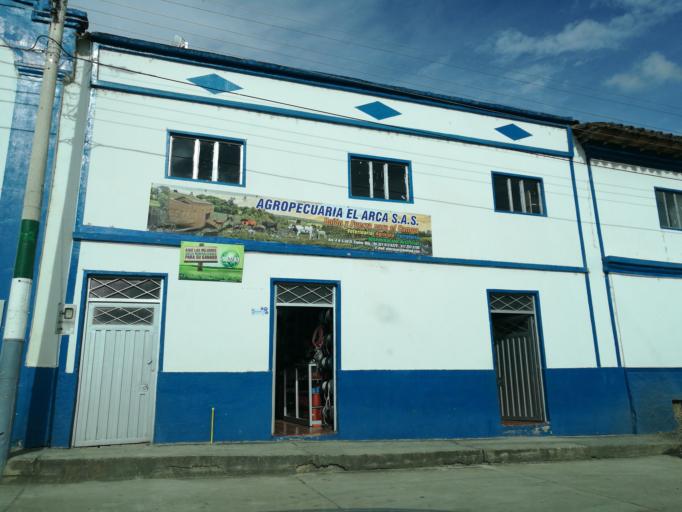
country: CO
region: Boyaca
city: El Espino
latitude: 6.4833
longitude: -72.4966
